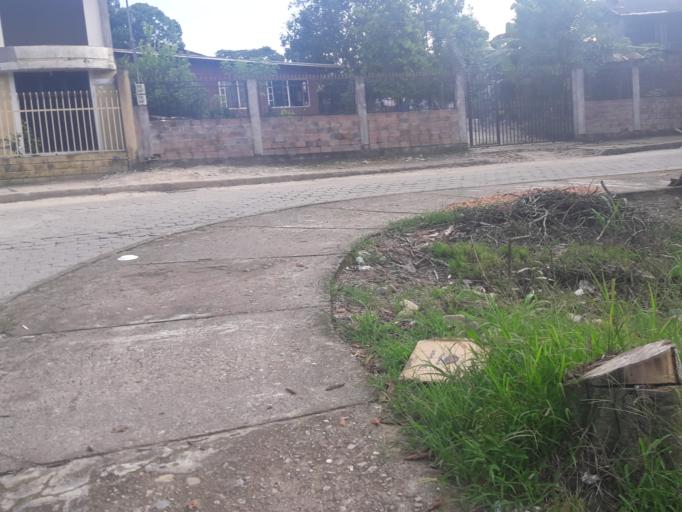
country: EC
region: Napo
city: Tena
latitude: -0.9896
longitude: -77.8092
